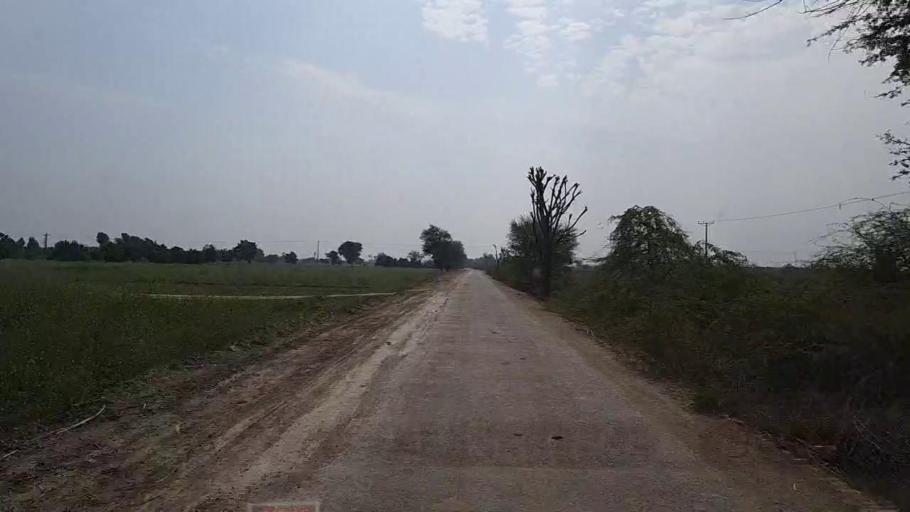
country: PK
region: Sindh
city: Mirwah Gorchani
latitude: 25.3437
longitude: 69.0536
